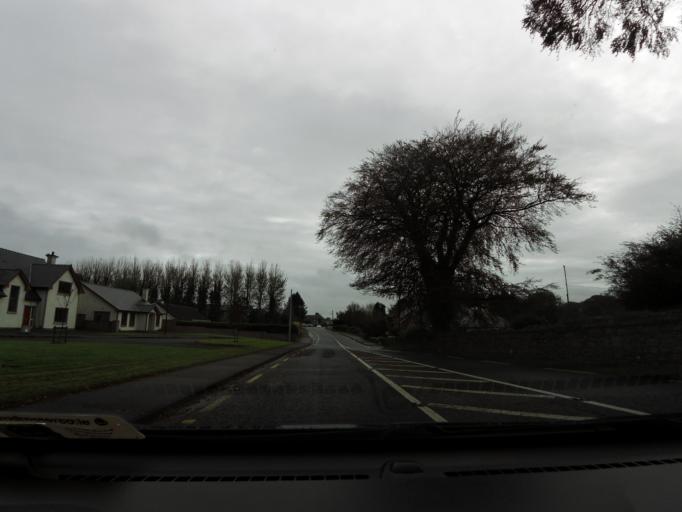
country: IE
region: Connaught
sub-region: County Galway
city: Tuam
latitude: 53.6155
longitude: -8.7486
